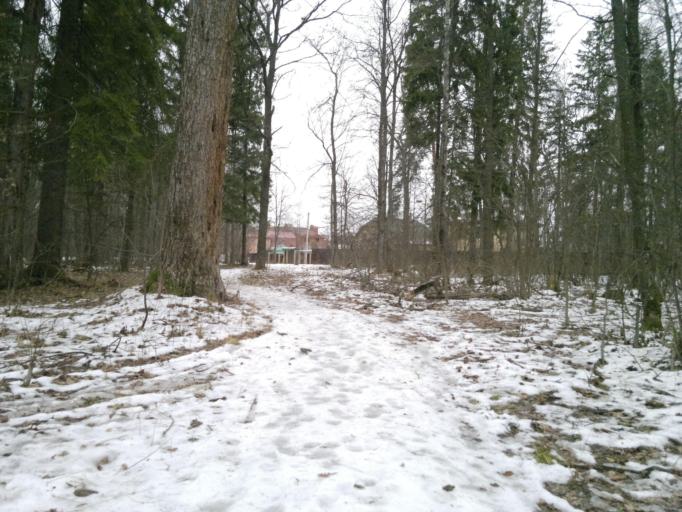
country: RU
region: Mariy-El
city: Yoshkar-Ola
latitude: 56.6144
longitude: 47.9450
